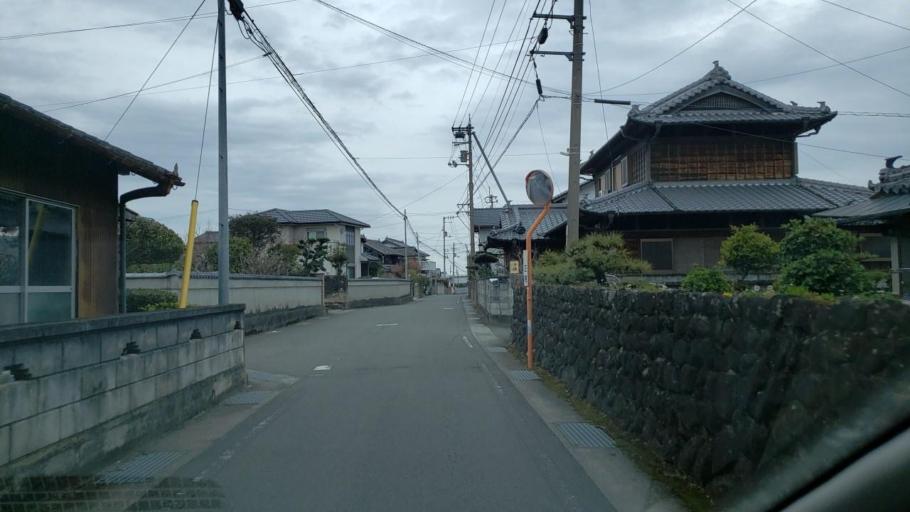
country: JP
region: Tokushima
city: Kamojimacho-jogejima
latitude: 34.0900
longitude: 134.2966
